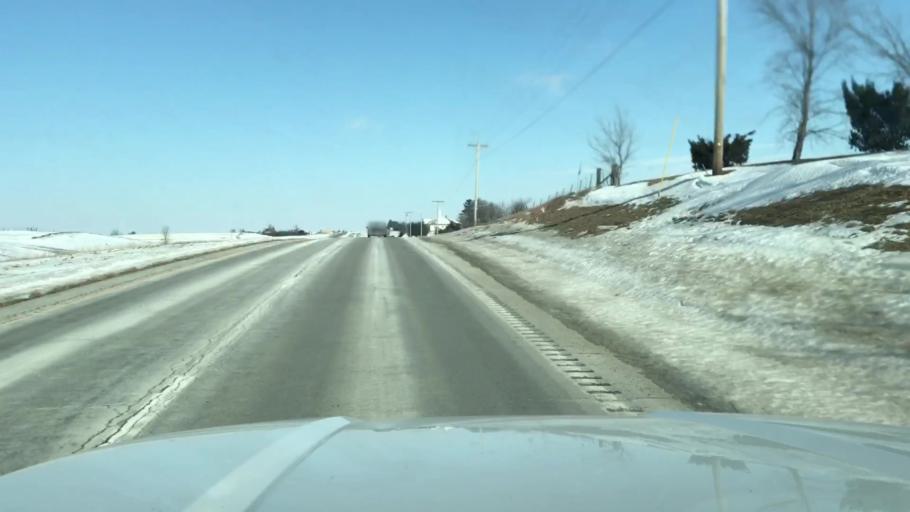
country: US
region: Missouri
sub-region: Andrew County
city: Savannah
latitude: 40.0122
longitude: -94.8796
